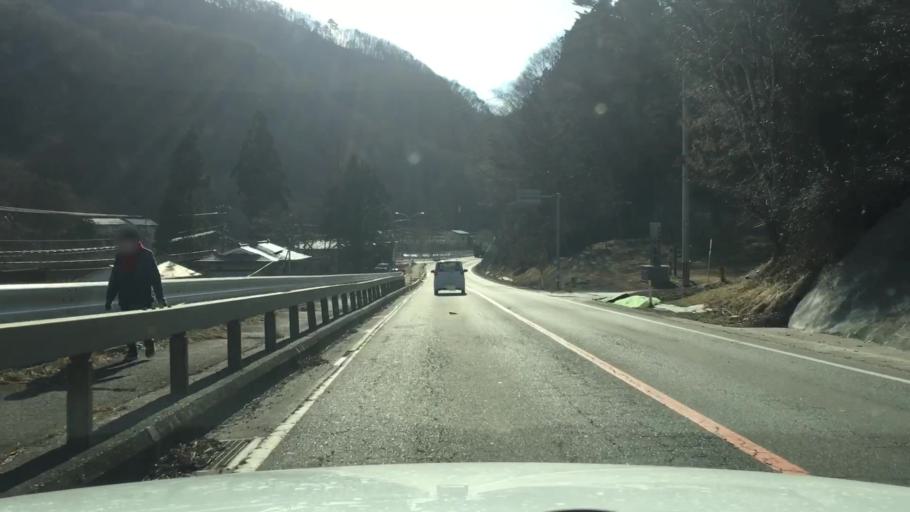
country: JP
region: Iwate
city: Miyako
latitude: 39.5947
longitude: 141.6761
